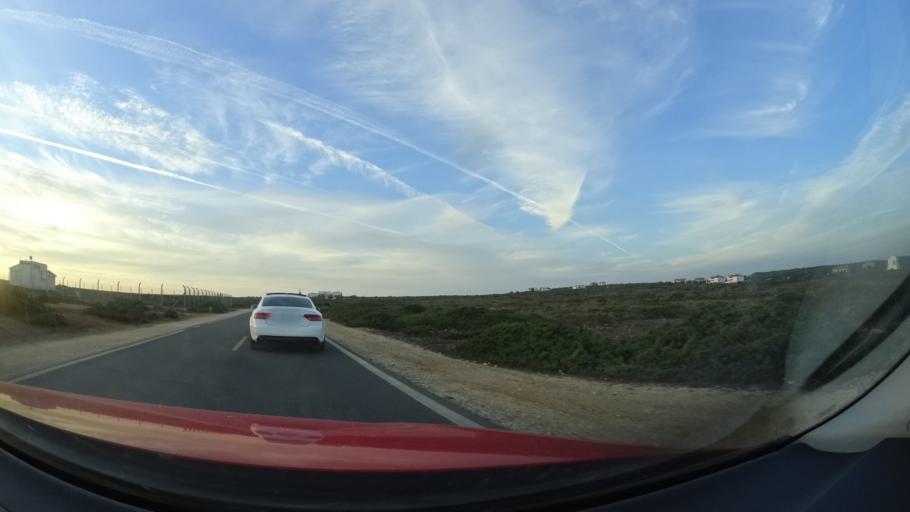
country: PT
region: Faro
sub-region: Vila do Bispo
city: Sagres
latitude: 37.0216
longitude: -8.9593
